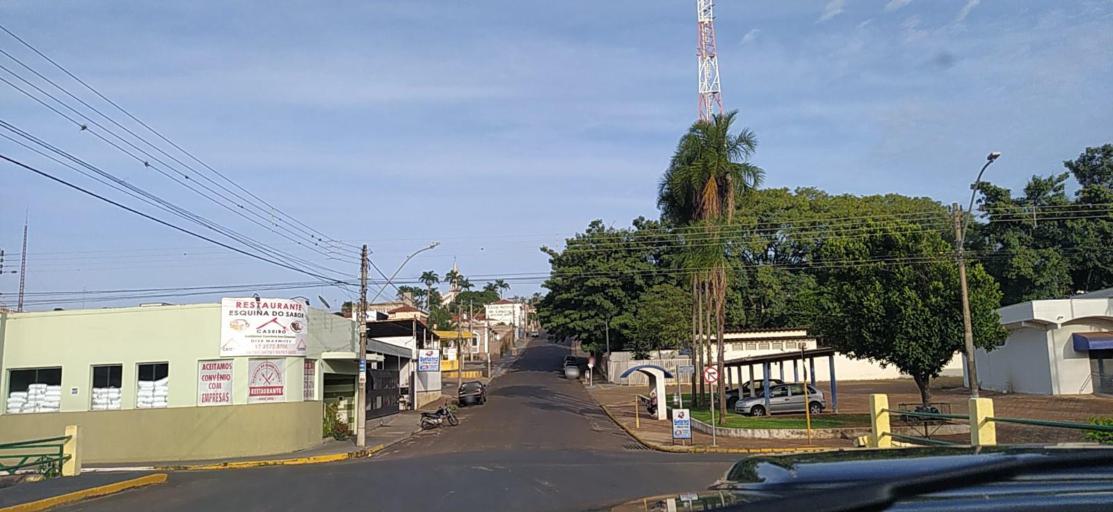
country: BR
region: Sao Paulo
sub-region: Pindorama
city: Pindorama
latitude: -21.1876
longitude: -48.9047
